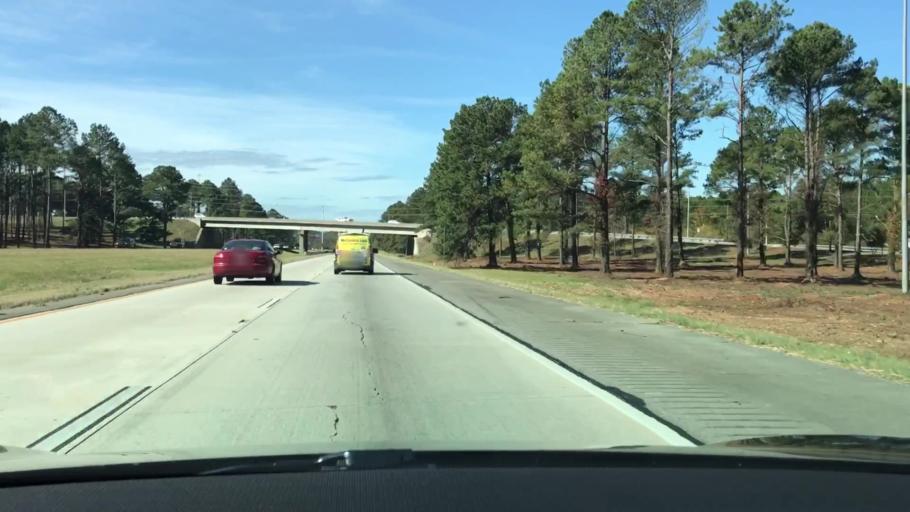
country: US
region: Georgia
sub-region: Greene County
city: Greensboro
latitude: 33.5461
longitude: -83.2028
